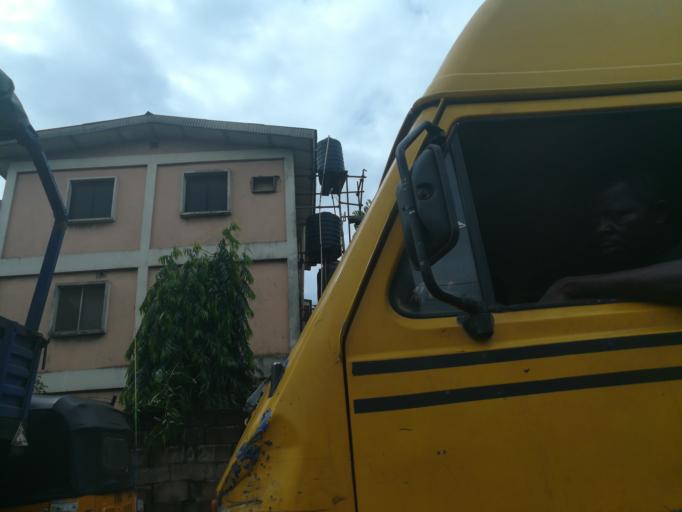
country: NG
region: Lagos
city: Agege
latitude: 6.6241
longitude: 3.3283
